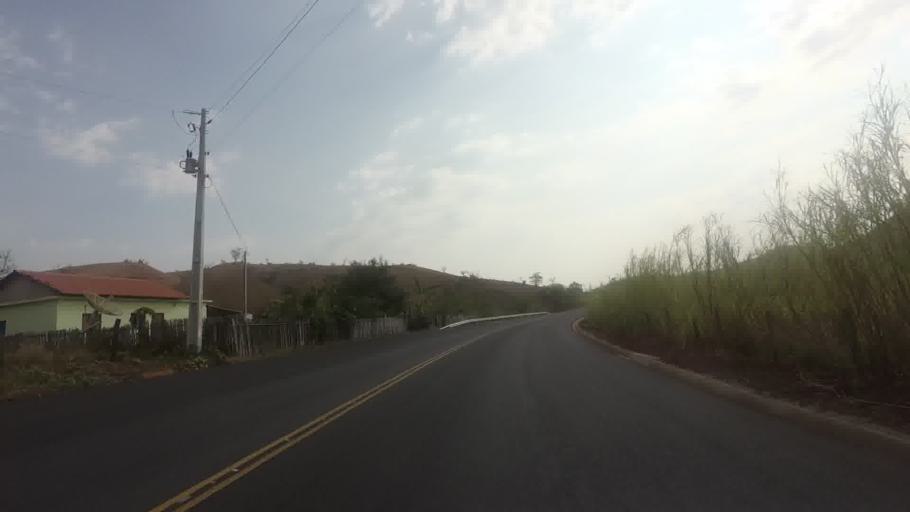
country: BR
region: Rio de Janeiro
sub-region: Itaperuna
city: Itaperuna
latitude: -21.3076
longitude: -41.8510
